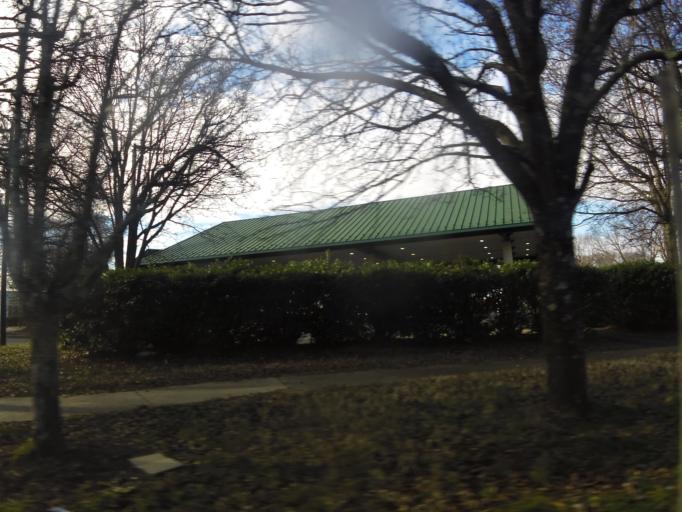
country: US
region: Virginia
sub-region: Henrico County
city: Short Pump
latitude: 37.6486
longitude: -77.5815
